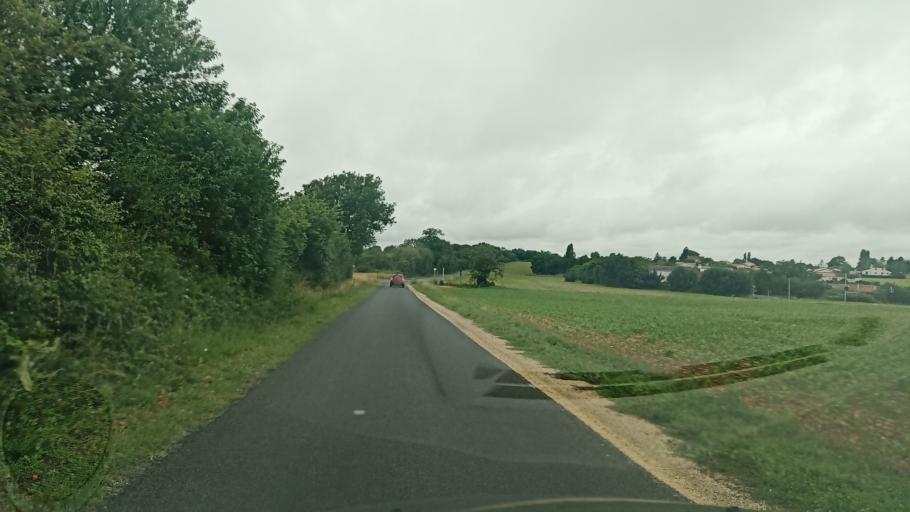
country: FR
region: Poitou-Charentes
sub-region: Departement de la Vienne
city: Biard
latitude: 46.5926
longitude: 0.2872
